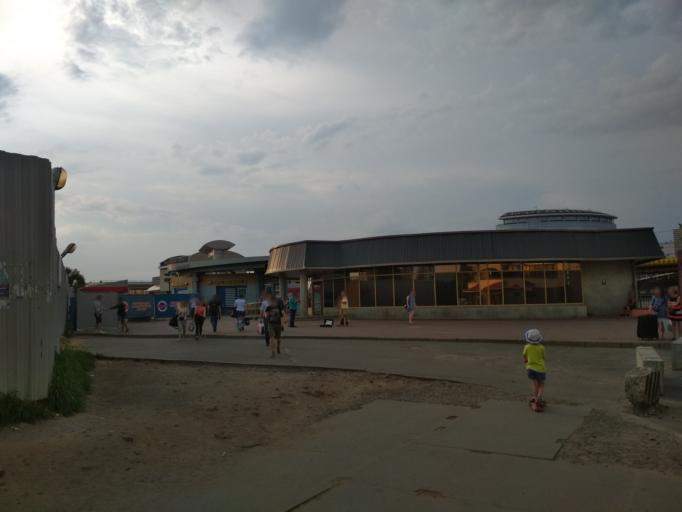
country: BY
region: Minsk
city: Minsk
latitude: 53.8892
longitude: 27.5500
